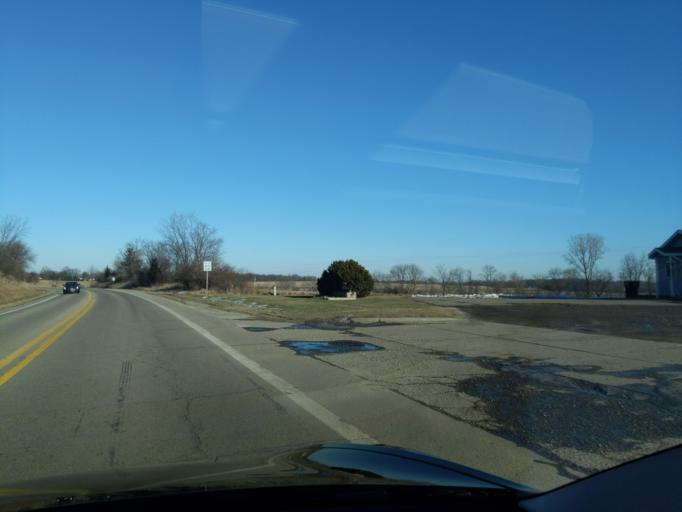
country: US
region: Michigan
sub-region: Ingham County
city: Stockbridge
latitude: 42.3951
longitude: -84.2483
